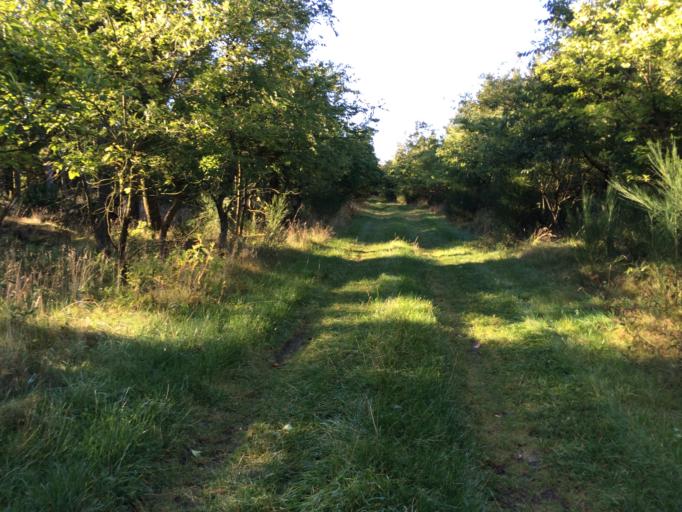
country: DK
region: Central Jutland
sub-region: Holstebro Kommune
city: Ulfborg
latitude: 56.2456
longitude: 8.3679
